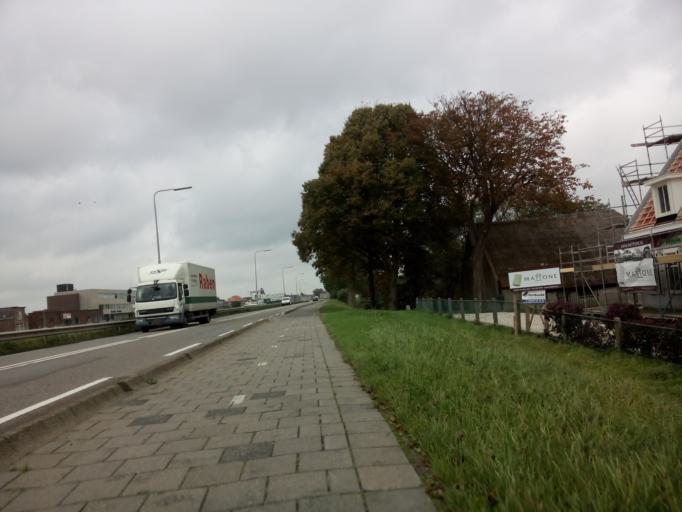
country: NL
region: South Holland
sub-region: Gemeente Waddinxveen
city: Waddinxveen
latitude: 52.0330
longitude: 4.6597
